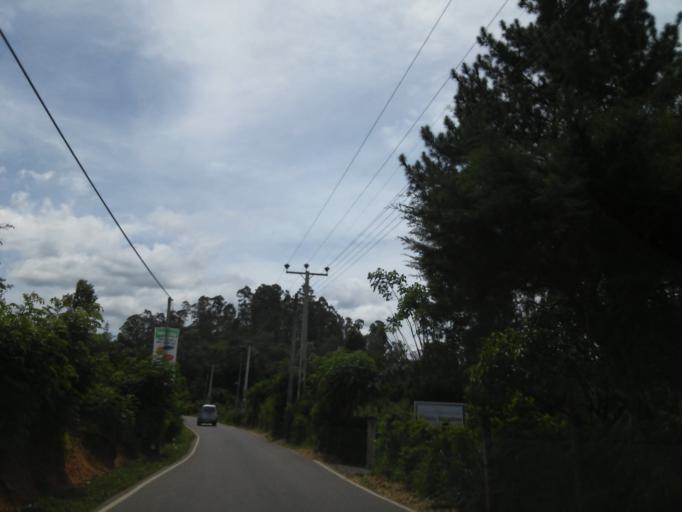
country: LK
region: Uva
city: Haputale
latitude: 6.8427
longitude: 81.0170
